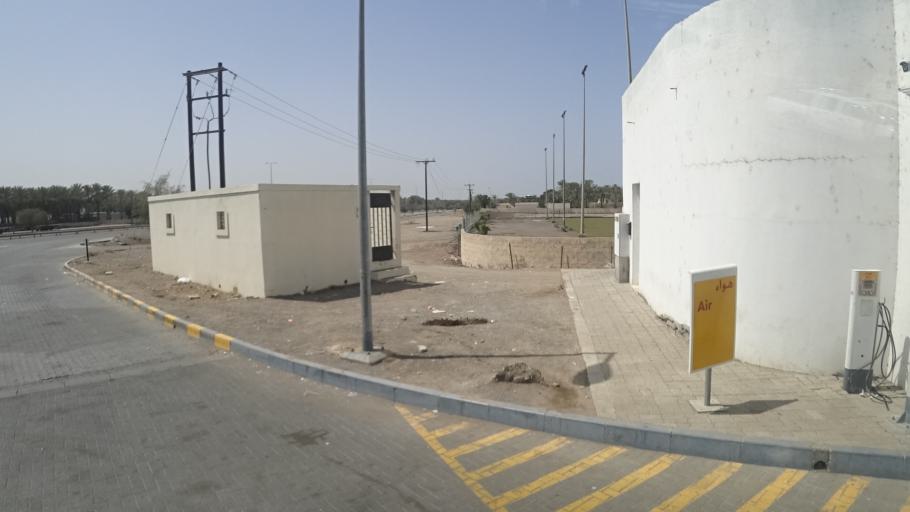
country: OM
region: Al Batinah
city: As Suwayq
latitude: 23.8691
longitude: 57.3065
